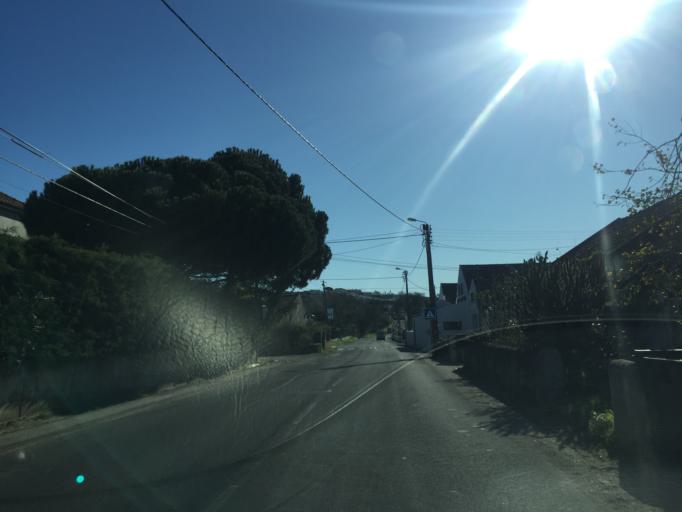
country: PT
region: Lisbon
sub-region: Sintra
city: Almargem
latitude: 38.8299
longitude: -9.3037
